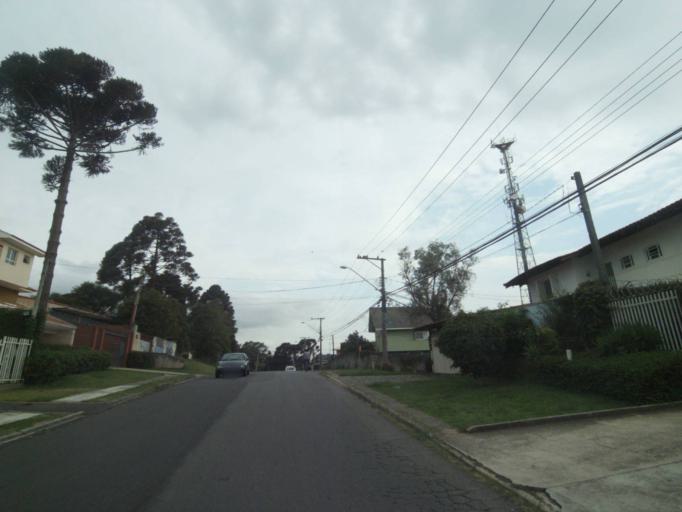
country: BR
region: Parana
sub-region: Curitiba
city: Curitiba
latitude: -25.3949
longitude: -49.2952
